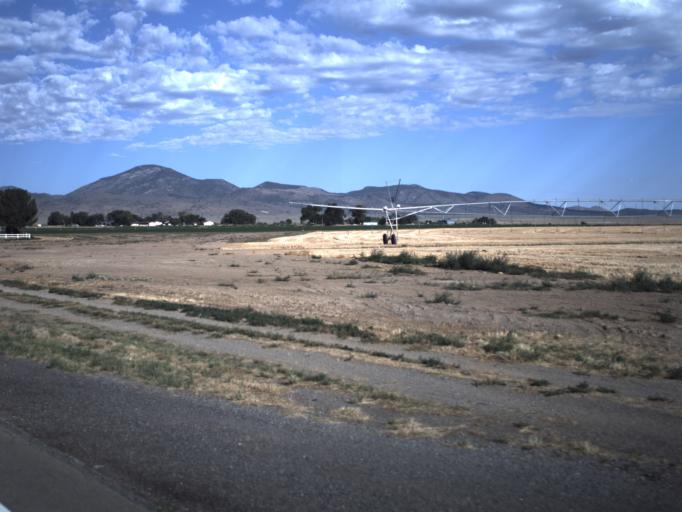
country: US
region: Utah
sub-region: Utah County
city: Genola
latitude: 39.9522
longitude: -111.9444
